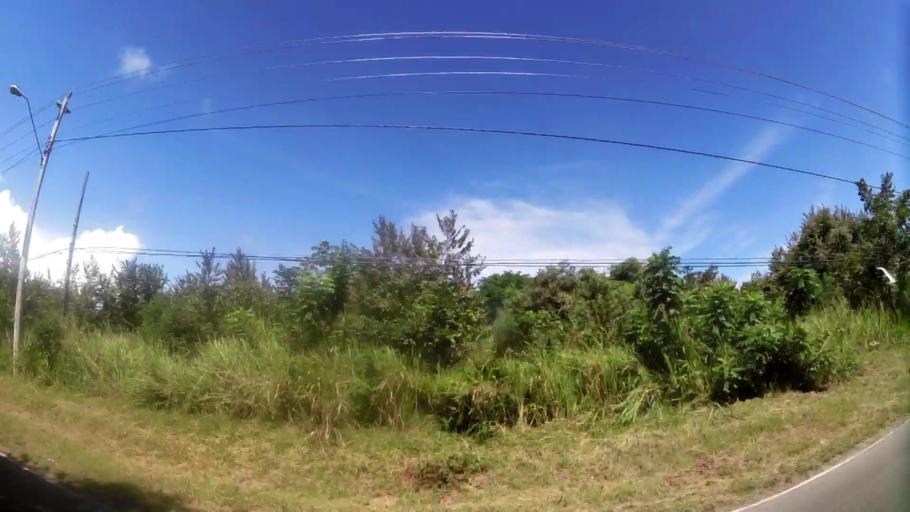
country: PA
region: Panama
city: Nueva Gorgona
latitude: 8.5579
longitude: -79.8765
